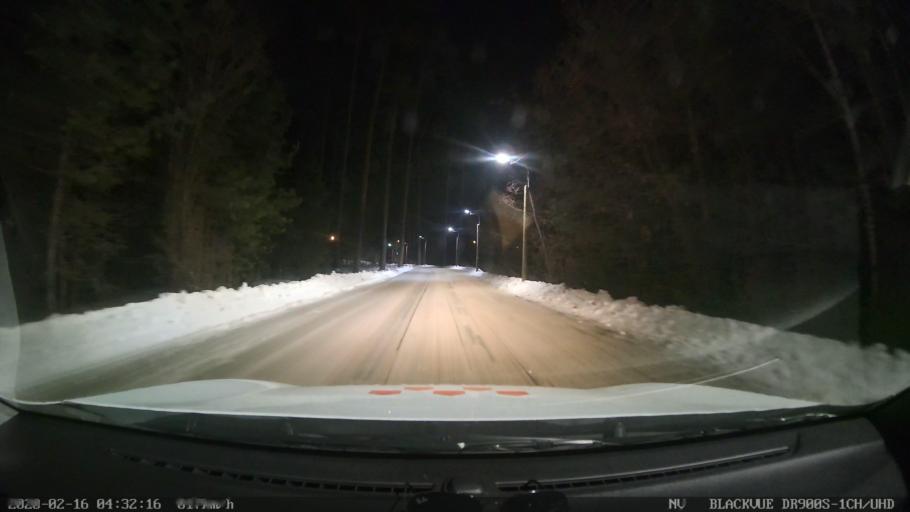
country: RU
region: Tatarstan
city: Staroye Arakchino
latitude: 55.8356
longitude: 48.9654
